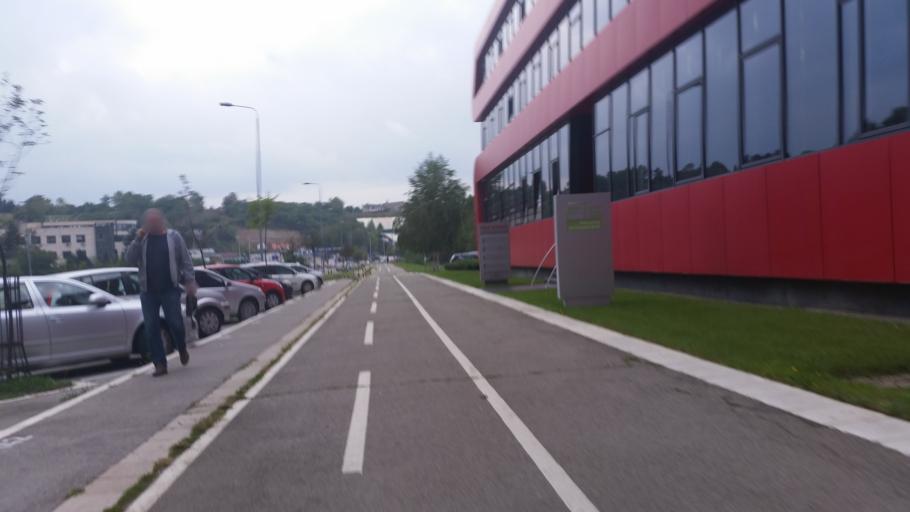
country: RS
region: Central Serbia
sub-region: Belgrade
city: Zemun
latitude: 44.8179
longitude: 20.3991
